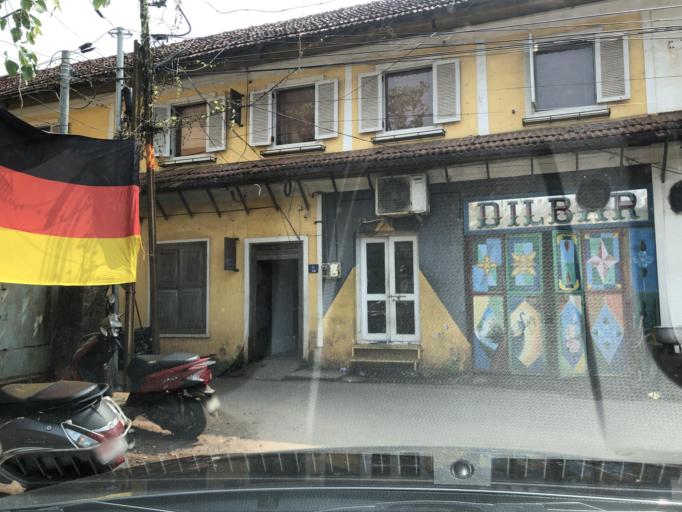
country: IN
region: Kerala
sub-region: Kozhikode
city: Kozhikode
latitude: 11.2474
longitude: 75.7738
